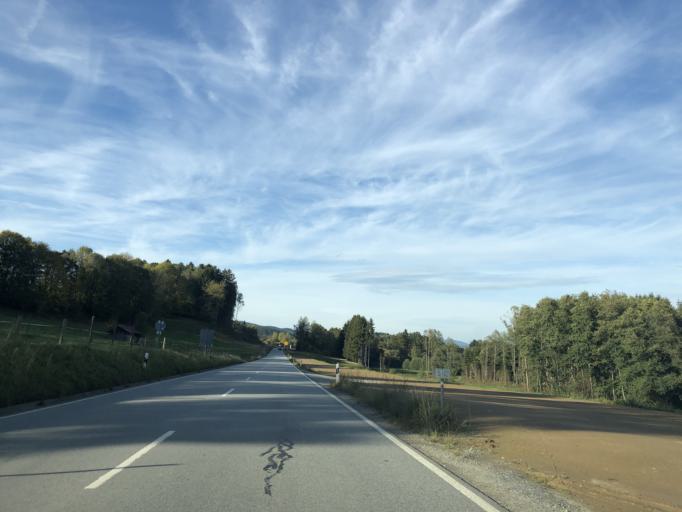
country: DE
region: Bavaria
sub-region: Lower Bavaria
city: Gotteszell
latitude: 48.9522
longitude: 12.9774
